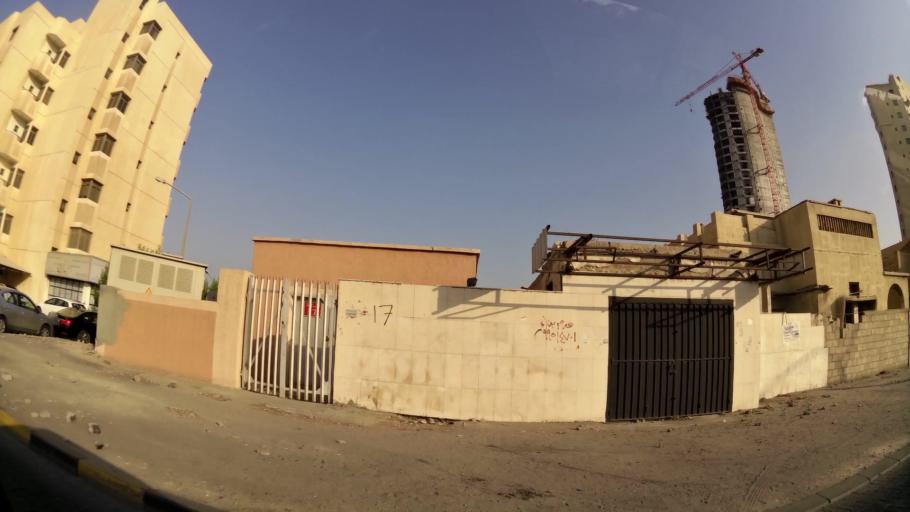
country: KW
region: Muhafazat Hawalli
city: As Salimiyah
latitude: 29.3385
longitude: 48.0626
